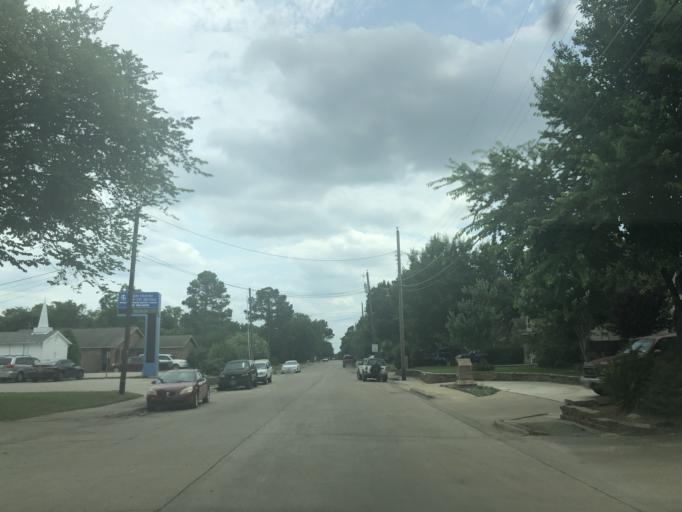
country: US
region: Texas
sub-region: Dallas County
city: Irving
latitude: 32.8083
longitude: -96.9300
